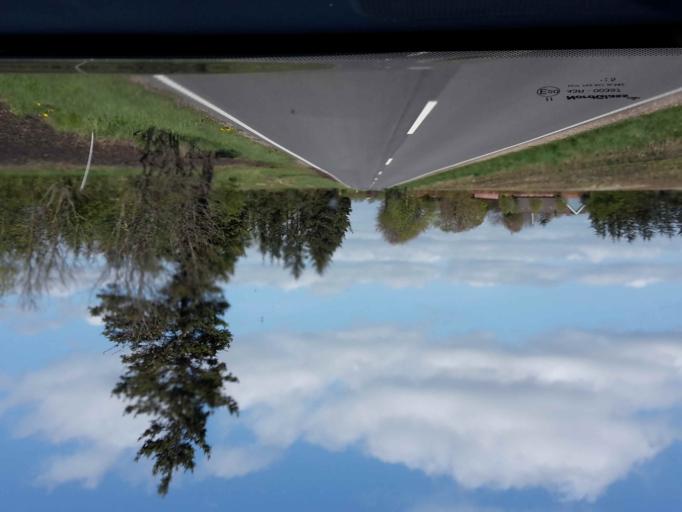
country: DK
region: South Denmark
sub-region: Billund Kommune
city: Grindsted
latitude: 55.6857
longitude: 8.8838
